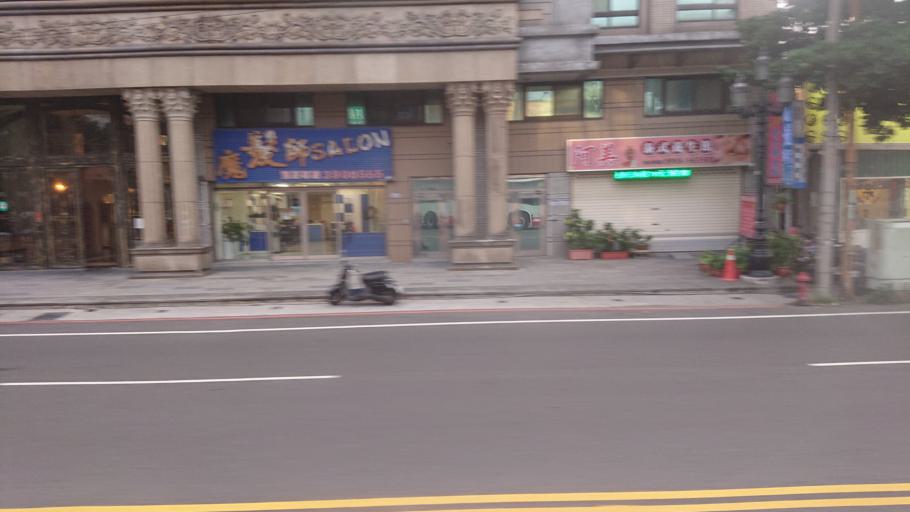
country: TW
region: Taiwan
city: Daxi
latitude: 24.8872
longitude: 121.2701
